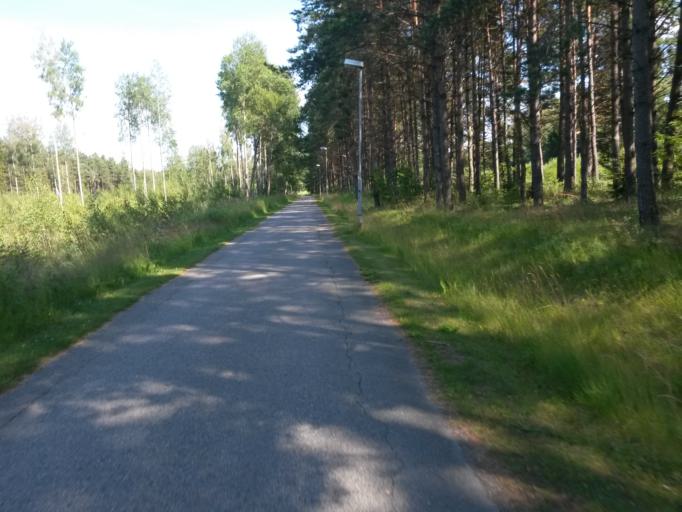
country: SE
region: Vaestra Goetaland
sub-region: Lidkopings Kommun
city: Lidkoping
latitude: 58.4950
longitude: 13.2052
